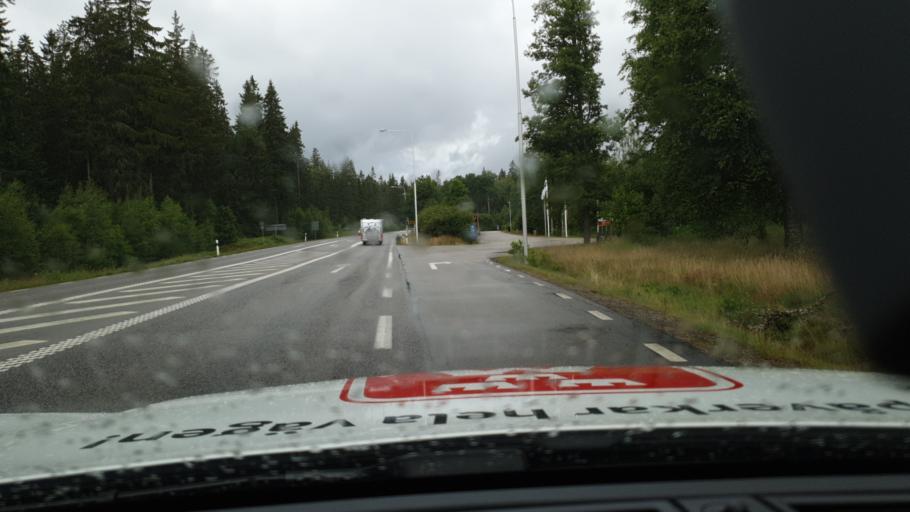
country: SE
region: Kronoberg
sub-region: Vaxjo Kommun
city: Lammhult
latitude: 57.1359
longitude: 14.6109
